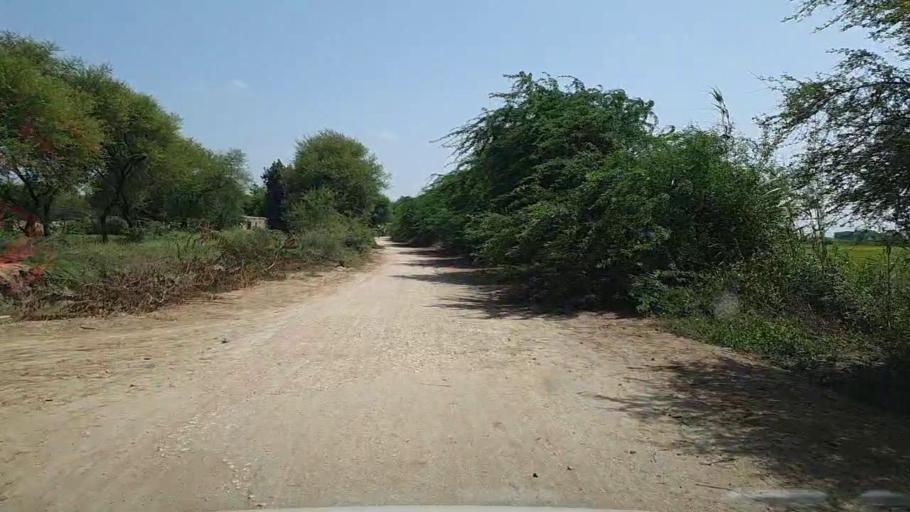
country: PK
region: Sindh
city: Kario
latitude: 24.8455
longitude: 68.6972
